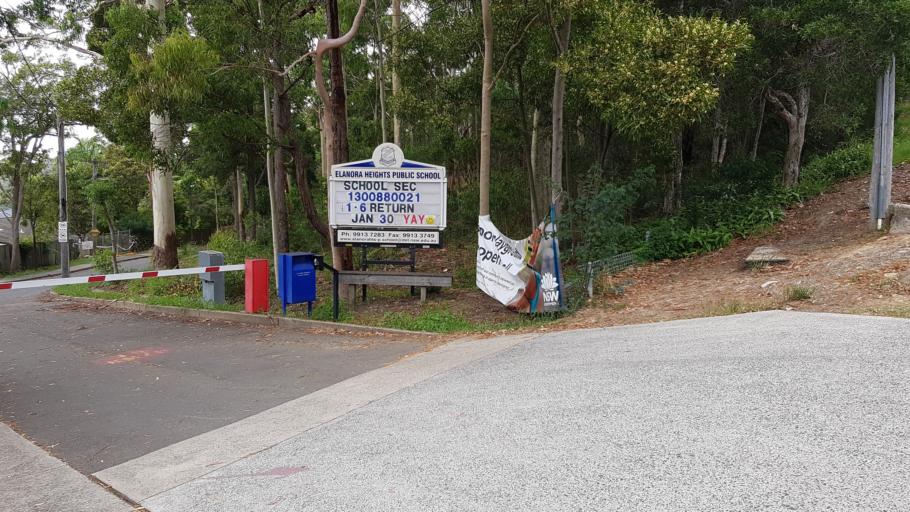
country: AU
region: New South Wales
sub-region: Pittwater
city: North Narrabeen
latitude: -33.7024
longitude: 151.2830
